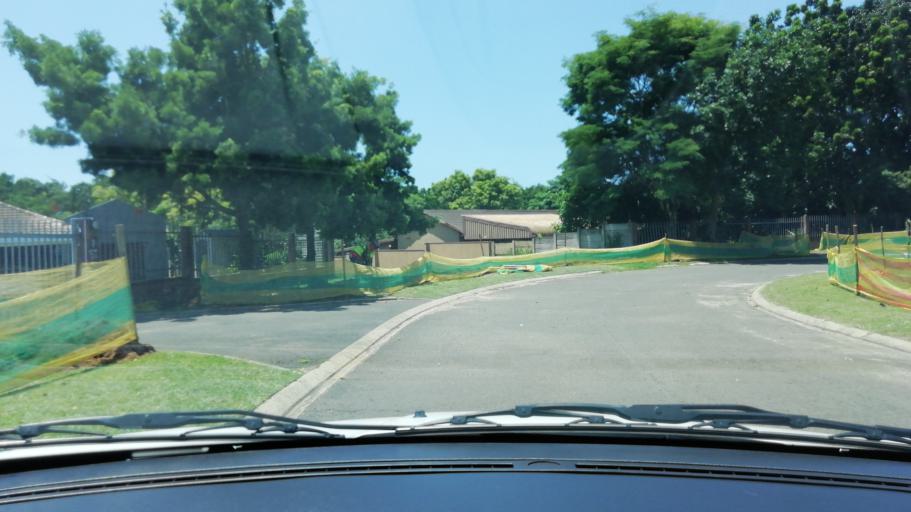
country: ZA
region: KwaZulu-Natal
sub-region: uThungulu District Municipality
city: Richards Bay
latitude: -28.7334
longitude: 32.0607
